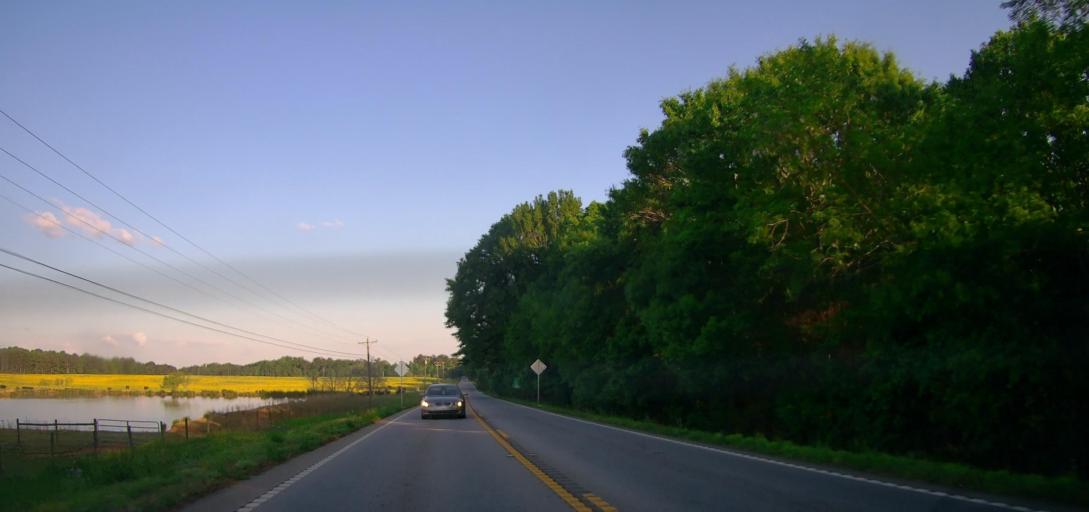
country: US
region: Georgia
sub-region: Walton County
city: Social Circle
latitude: 33.5518
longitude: -83.7375
